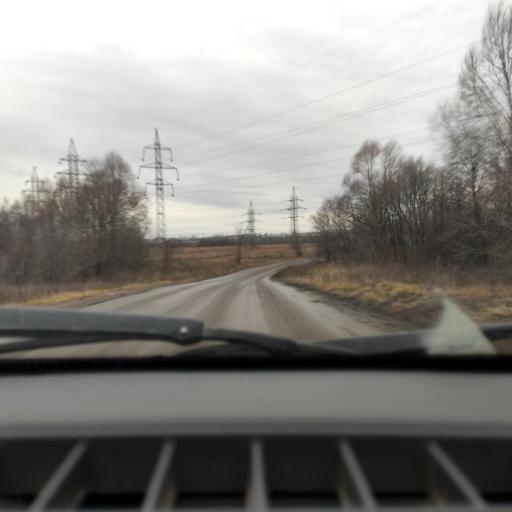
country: RU
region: Bashkortostan
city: Blagoveshchensk
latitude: 54.9403
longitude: 56.1001
